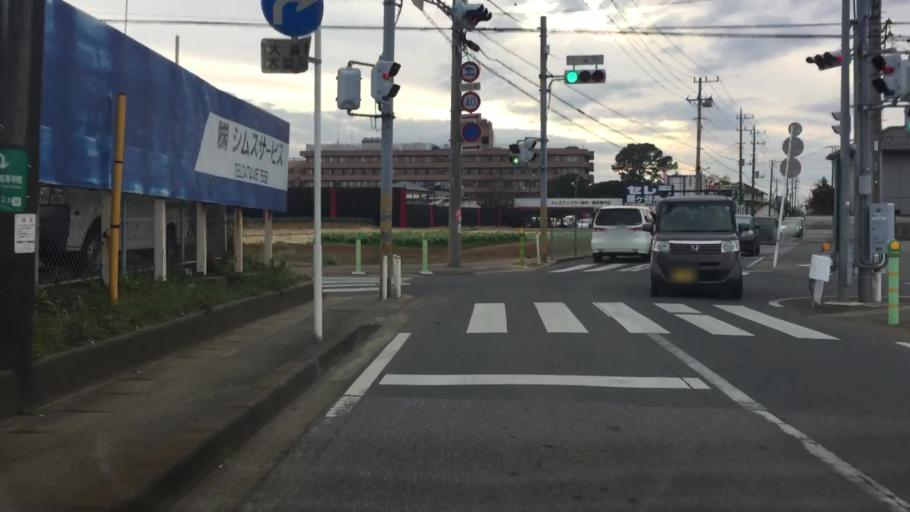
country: JP
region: Chiba
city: Kashiwa
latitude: 35.7867
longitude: 139.9880
